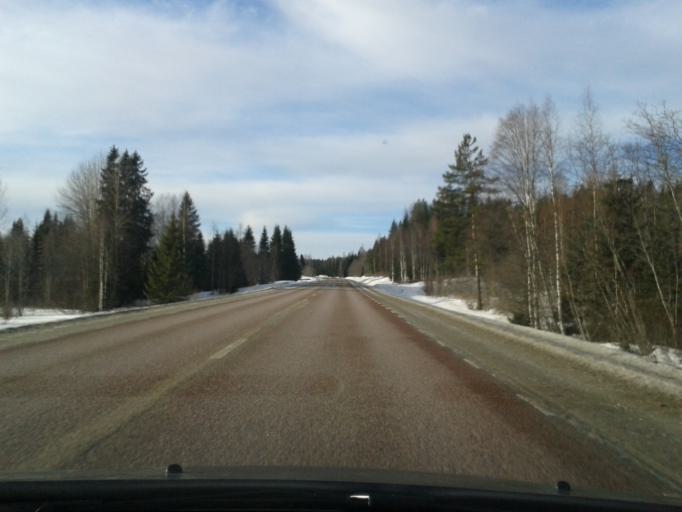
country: SE
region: Vaesternorrland
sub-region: OErnskoeldsviks Kommun
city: Bredbyn
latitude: 63.3929
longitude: 18.3344
